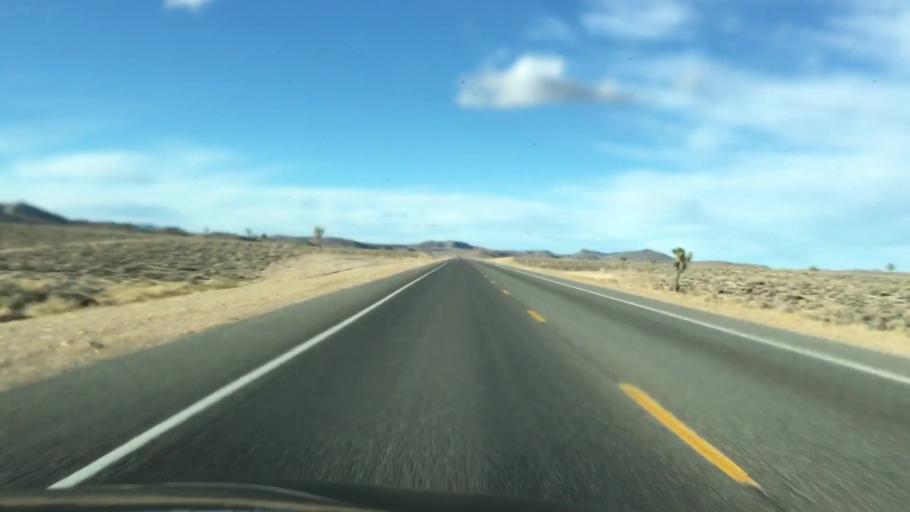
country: US
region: Nevada
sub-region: Esmeralda County
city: Goldfield
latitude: 37.5850
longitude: -117.2066
